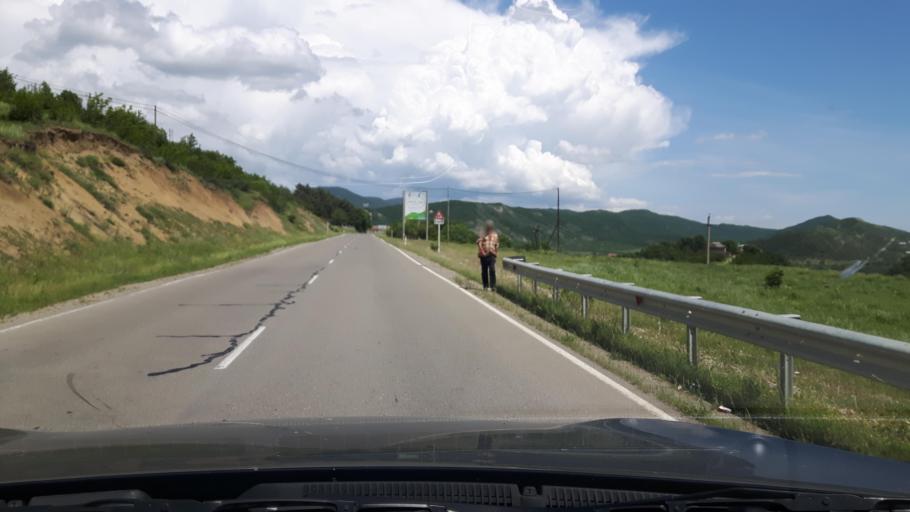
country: GE
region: Kakheti
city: Sagarejo
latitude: 41.7834
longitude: 45.1593
